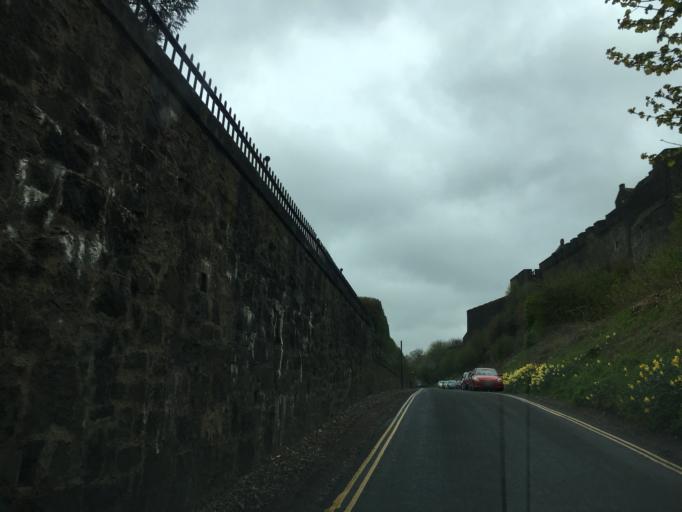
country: GB
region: Scotland
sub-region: Stirling
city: Stirling
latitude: 56.1253
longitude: -3.9479
